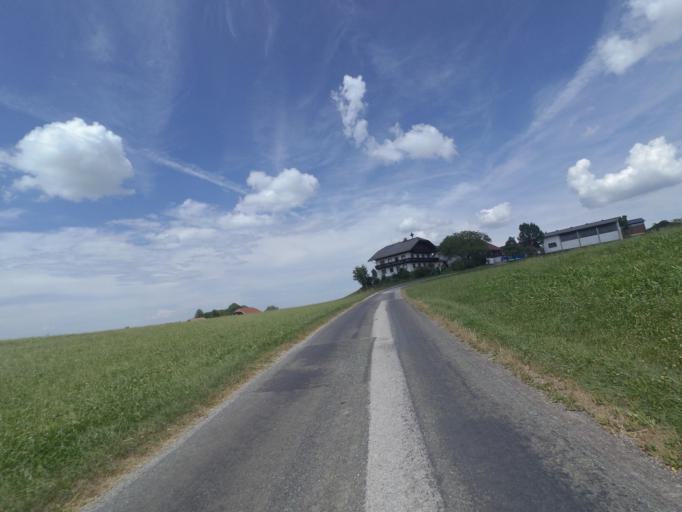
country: AT
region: Salzburg
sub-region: Politischer Bezirk Salzburg-Umgebung
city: Mattsee
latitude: 47.9715
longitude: 13.1274
